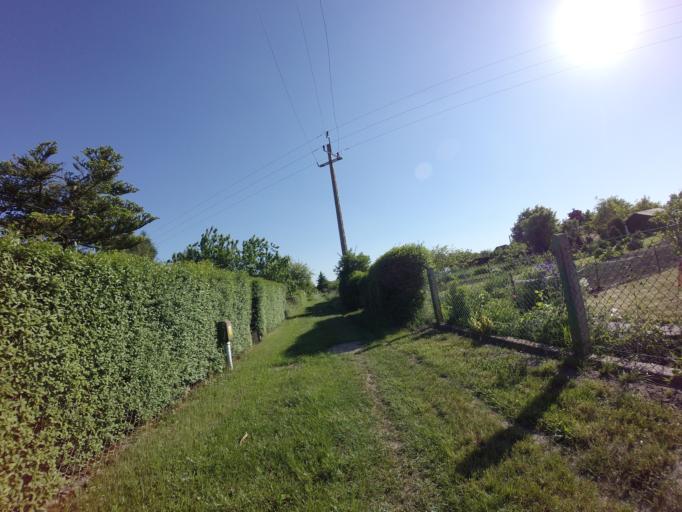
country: PL
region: West Pomeranian Voivodeship
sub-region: Powiat choszczenski
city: Choszczno
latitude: 53.1592
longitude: 15.3997
